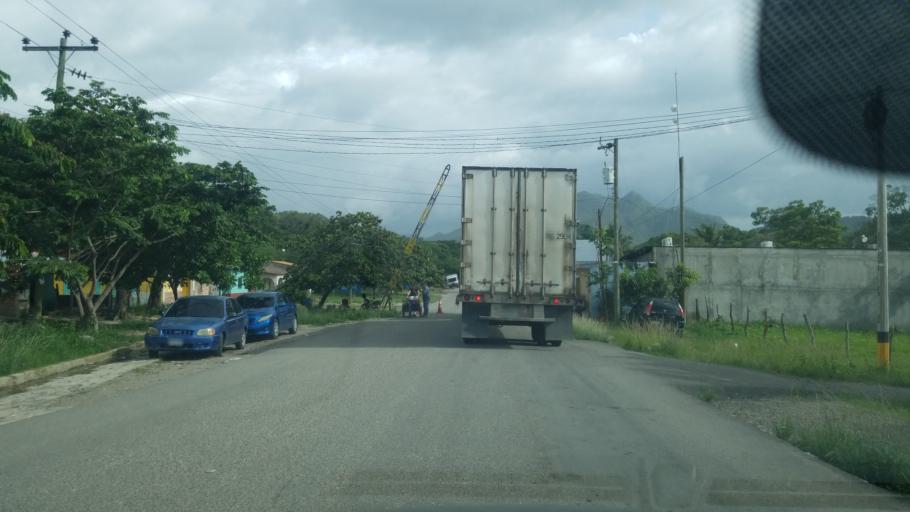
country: HN
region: Ocotepeque
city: Antigua Ocotepeque
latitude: 14.3776
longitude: -89.2089
